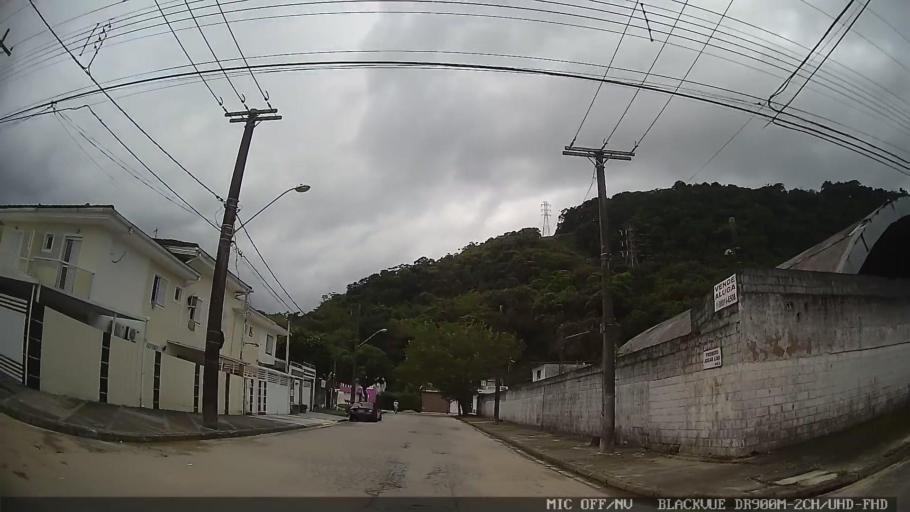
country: BR
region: Sao Paulo
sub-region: Guaruja
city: Guaruja
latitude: -23.9940
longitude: -46.2709
